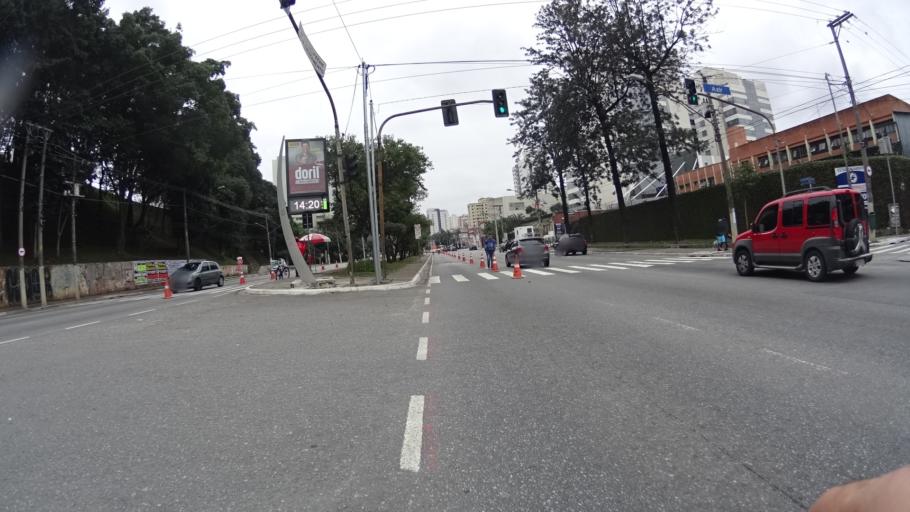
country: BR
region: Sao Paulo
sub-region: Sao Paulo
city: Sao Paulo
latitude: -23.4990
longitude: -46.6135
